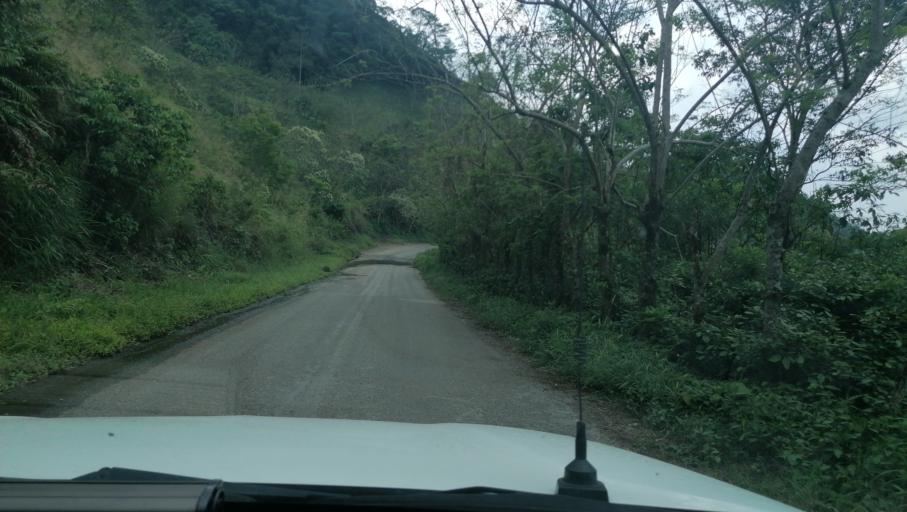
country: MX
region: Chiapas
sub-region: Francisco Leon
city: San Miguel la Sardina
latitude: 17.2369
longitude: -93.3112
